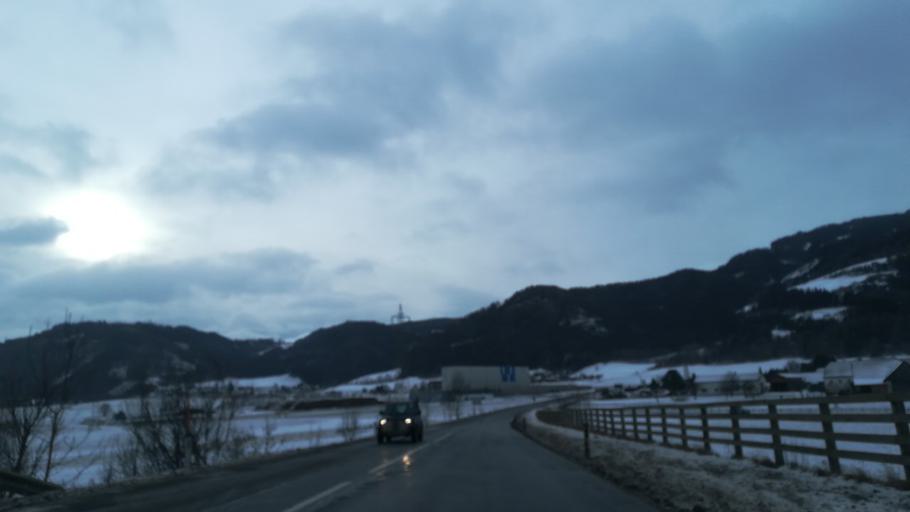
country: AT
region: Styria
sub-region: Politischer Bezirk Murtal
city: Sankt Peter ob Judenburg
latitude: 47.1893
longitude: 14.6001
